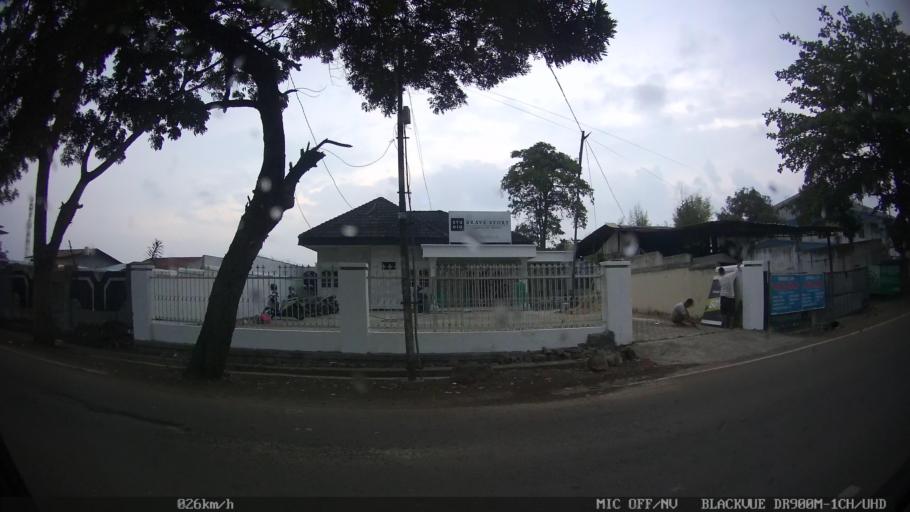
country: ID
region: Lampung
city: Kedaton
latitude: -5.3951
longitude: 105.2813
